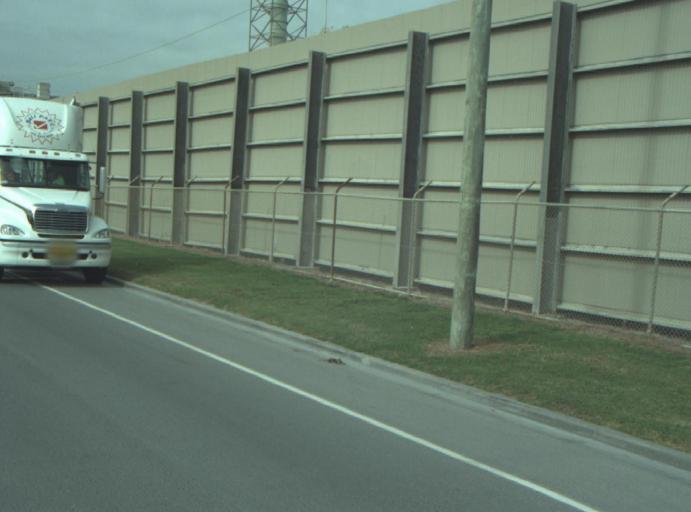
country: AU
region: Victoria
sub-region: Greater Geelong
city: Bell Park
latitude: -38.0952
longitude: 144.3807
